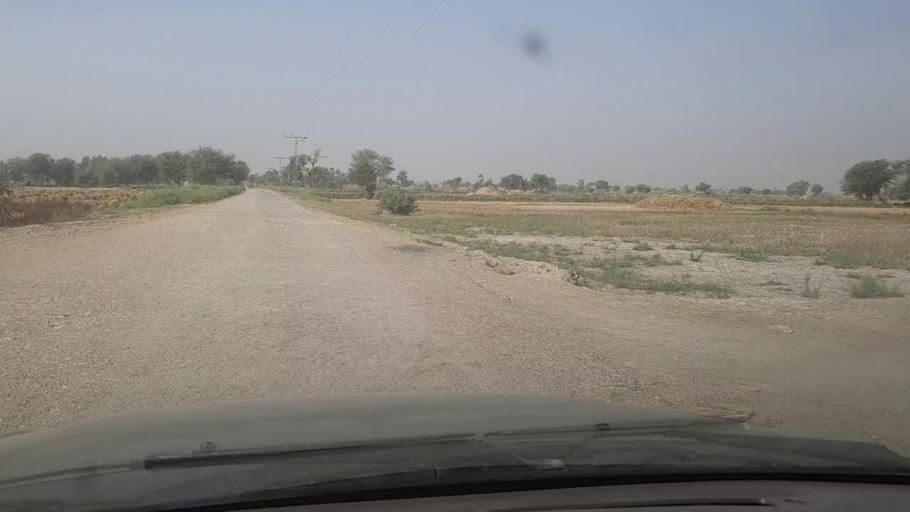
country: PK
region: Sindh
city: Garhi Yasin
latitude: 27.8759
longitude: 68.5632
